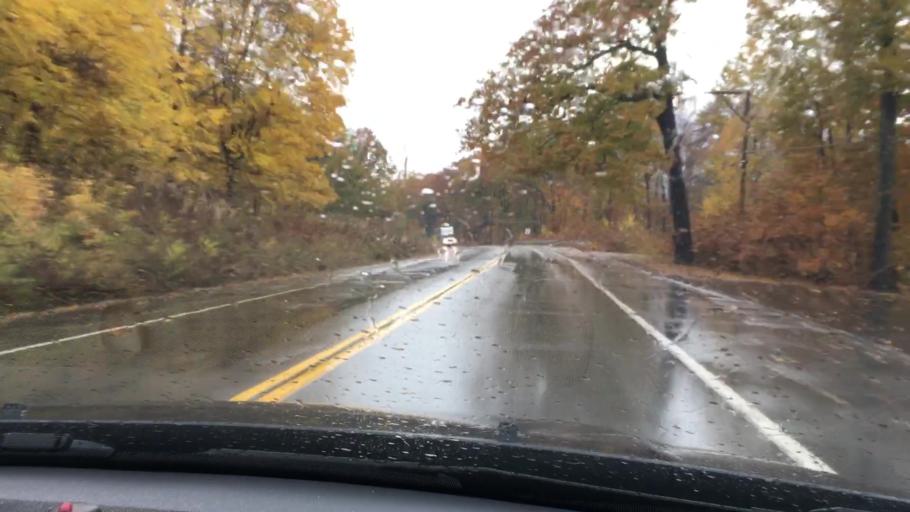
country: US
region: New Hampshire
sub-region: Grafton County
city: Holderness
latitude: 43.7315
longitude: -71.5783
